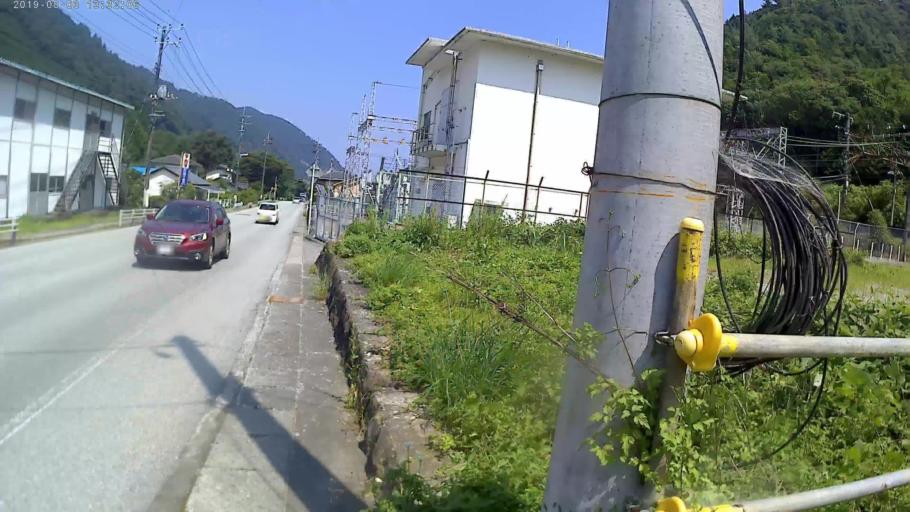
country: JP
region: Yamanashi
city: Otsuki
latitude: 35.6042
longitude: 138.8237
